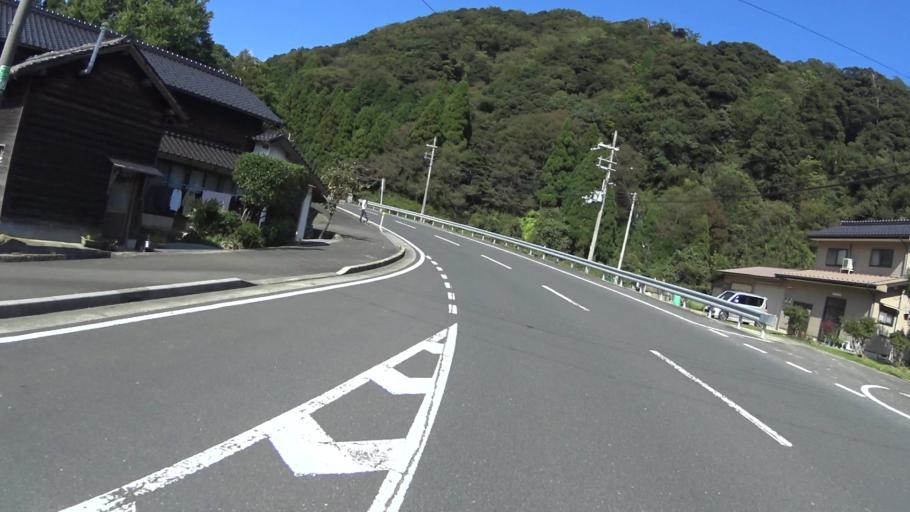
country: JP
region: Kyoto
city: Miyazu
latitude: 35.7319
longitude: 135.2583
